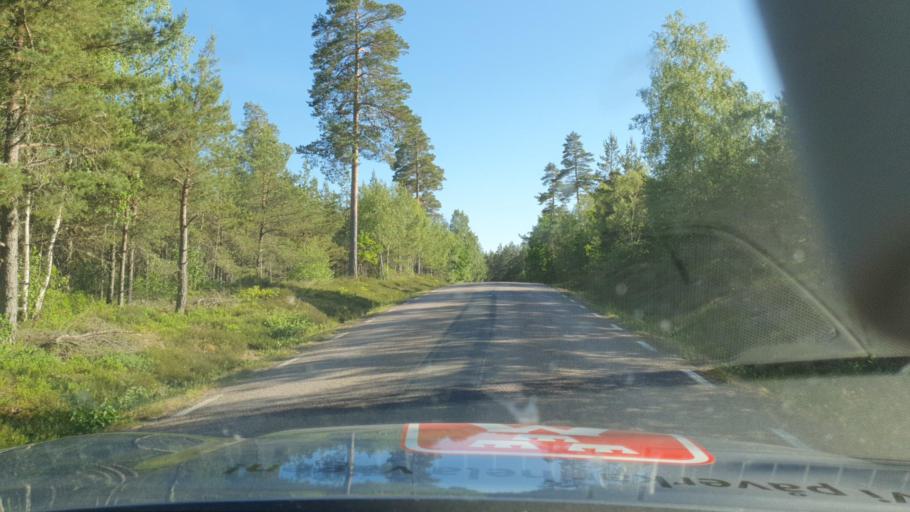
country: SE
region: Kalmar
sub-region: Torsas Kommun
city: Torsas
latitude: 56.4874
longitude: 16.0971
